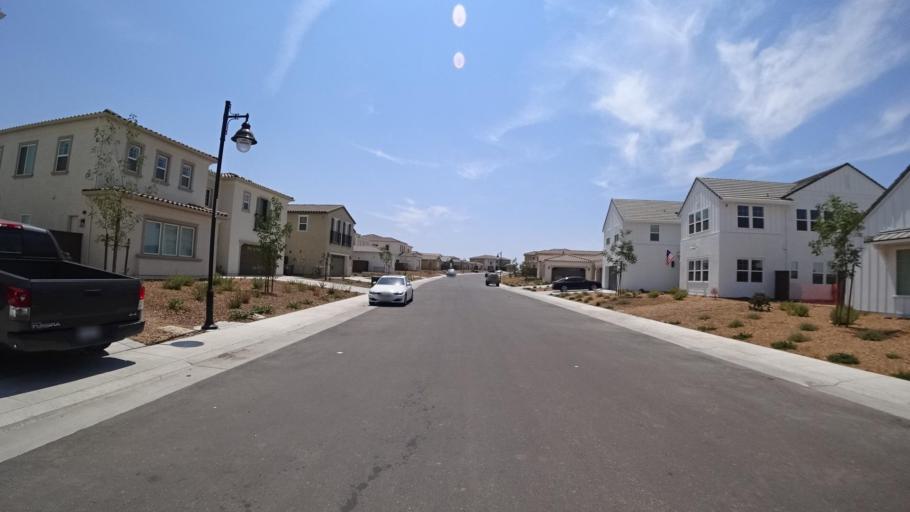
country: US
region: California
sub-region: Placer County
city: Rocklin
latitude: 38.8063
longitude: -121.2358
